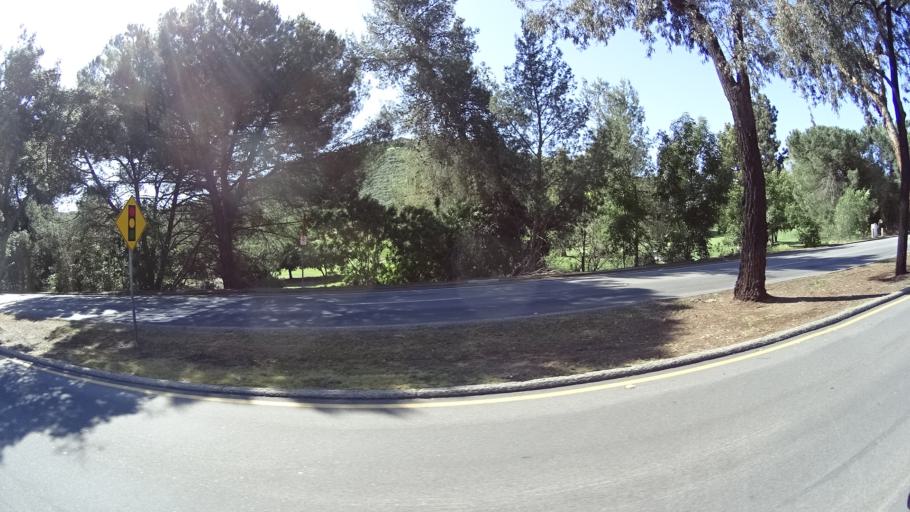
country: US
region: California
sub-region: Ventura County
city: Moorpark
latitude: 34.2377
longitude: -118.8508
